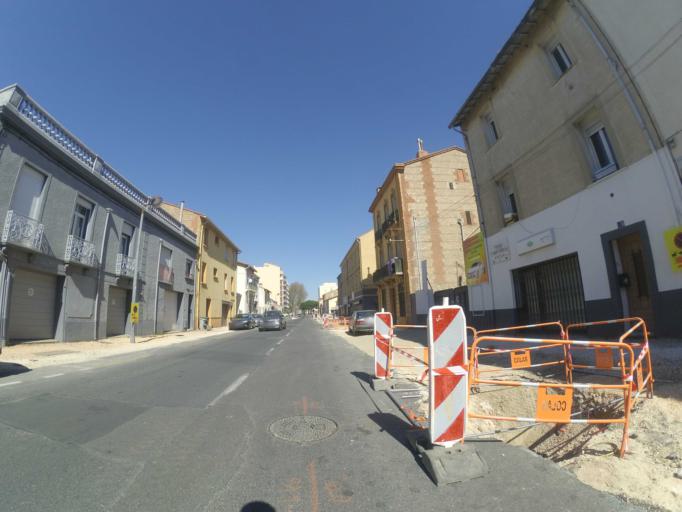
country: FR
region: Languedoc-Roussillon
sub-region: Departement des Pyrenees-Orientales
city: Perpignan
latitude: 42.7135
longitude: 2.8891
